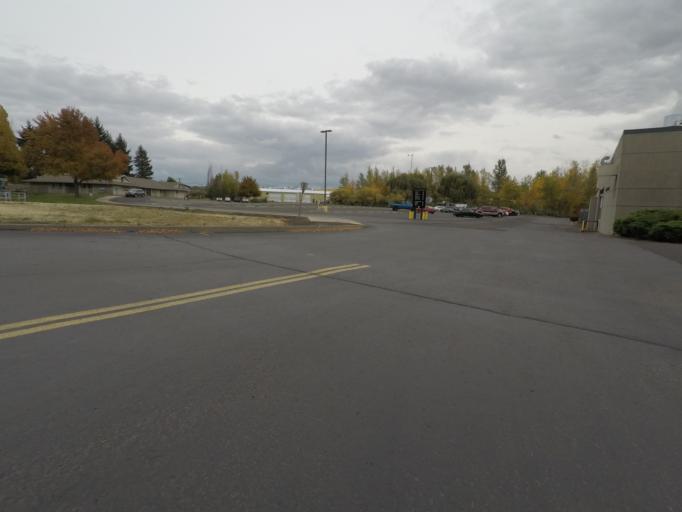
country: US
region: Washington
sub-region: Walla Walla County
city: Walla Walla East
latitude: 46.0801
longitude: -118.2753
